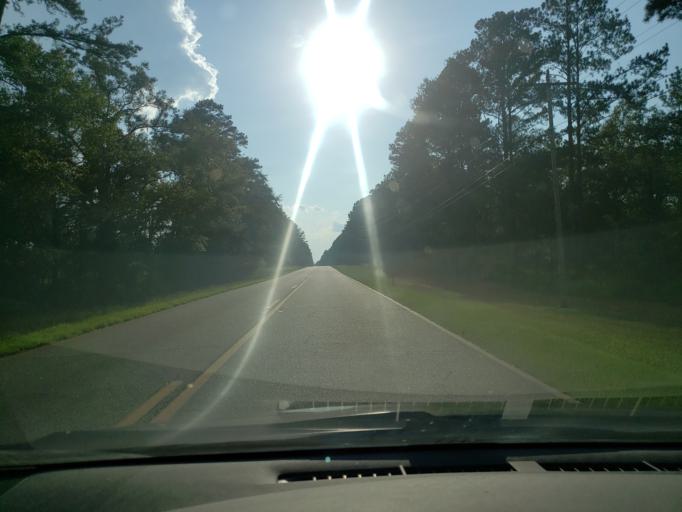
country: US
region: Georgia
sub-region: Terrell County
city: Dawson
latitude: 31.5774
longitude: -84.3750
